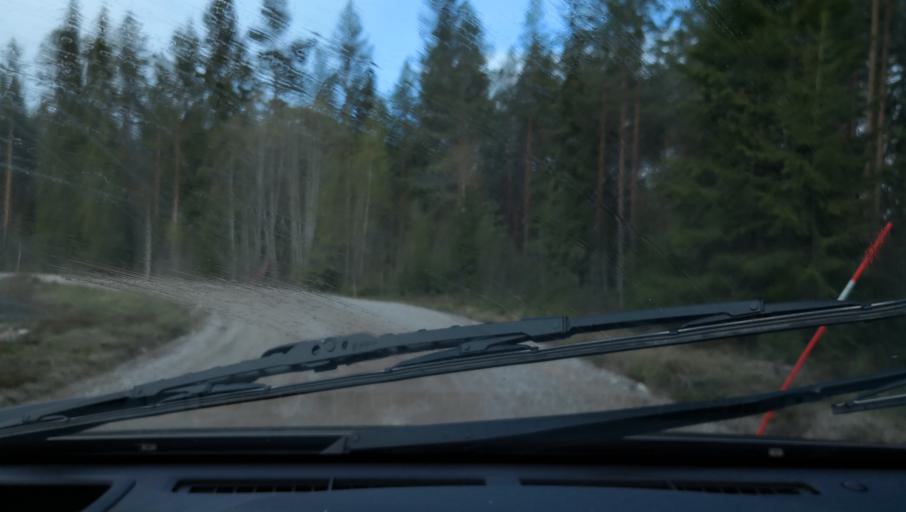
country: SE
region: Dalarna
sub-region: Saters Kommun
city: Saeter
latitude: 60.1710
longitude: 15.7248
